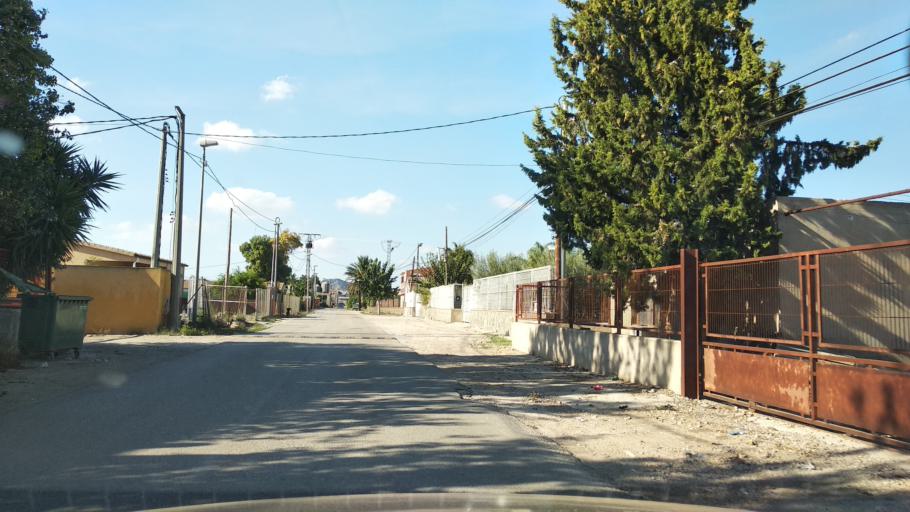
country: ES
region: Murcia
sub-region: Murcia
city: Santomera
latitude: 38.0521
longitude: -1.0411
